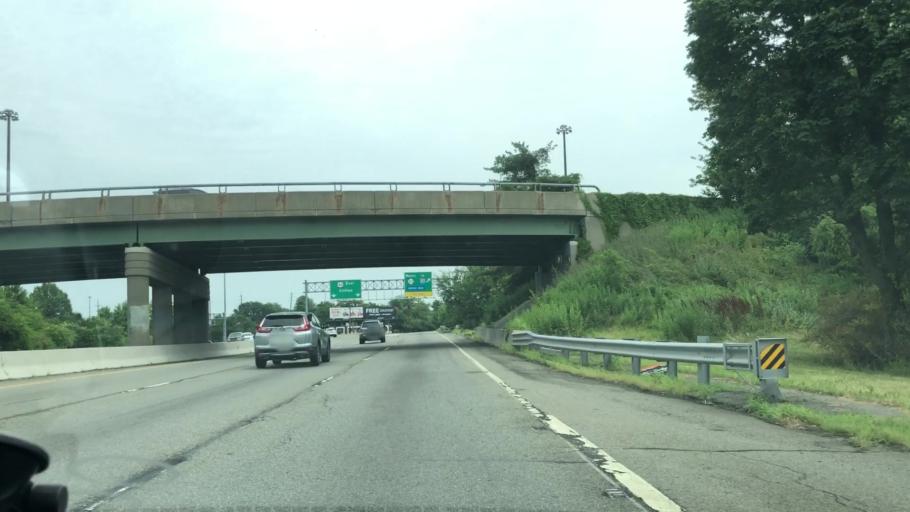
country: US
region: New Jersey
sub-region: Passaic County
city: Singac
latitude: 40.8931
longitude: -74.2561
